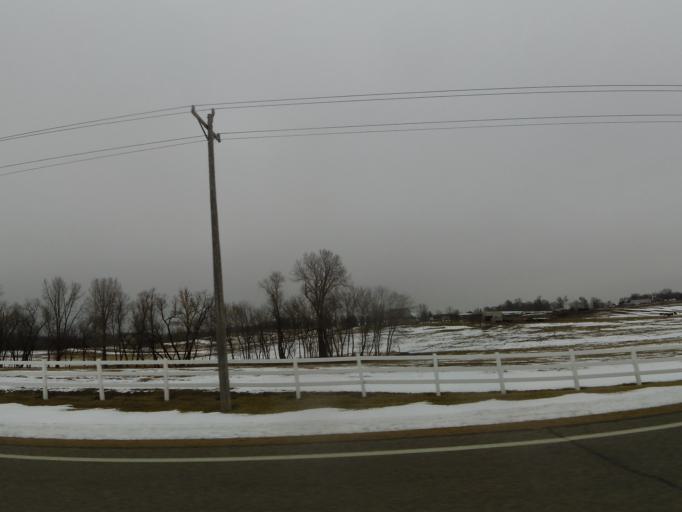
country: US
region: Minnesota
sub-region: Le Sueur County
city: New Prague
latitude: 44.6305
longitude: -93.5088
